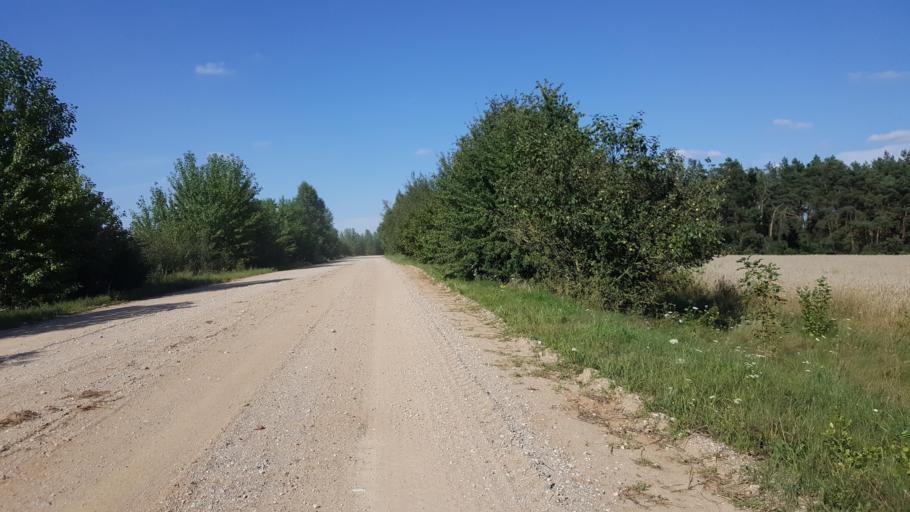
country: BY
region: Brest
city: Kamyanyets
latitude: 52.3544
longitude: 23.6933
